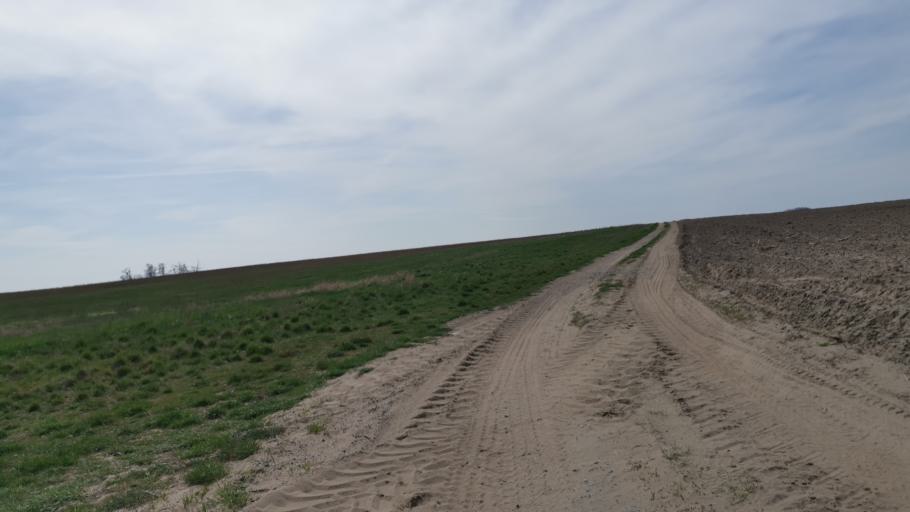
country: SK
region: Trnavsky
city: Gbely
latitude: 48.6759
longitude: 17.1190
